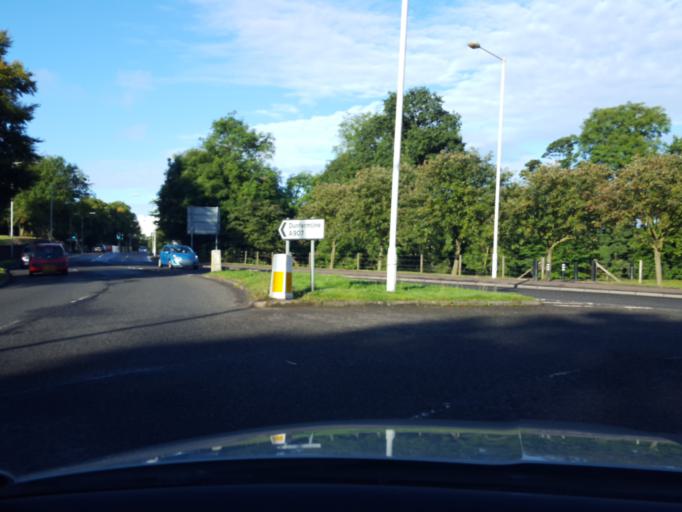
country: GB
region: Scotland
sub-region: Fife
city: Townhill
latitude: 56.0797
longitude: -3.4125
